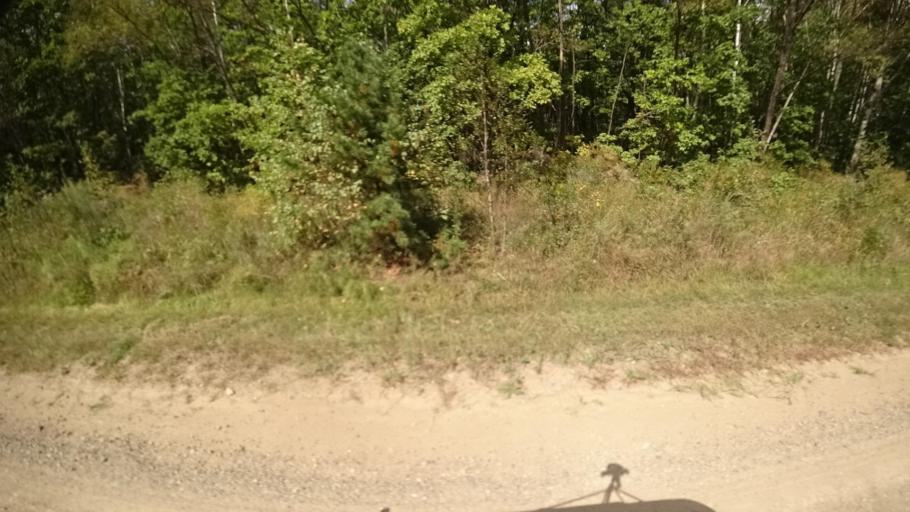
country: RU
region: Primorskiy
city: Yakovlevka
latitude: 44.6635
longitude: 133.6042
